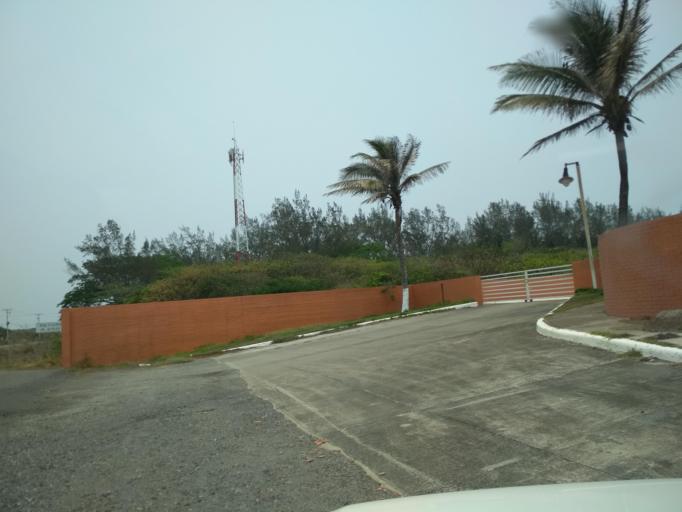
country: MX
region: Veracruz
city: Anton Lizardo
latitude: 19.0551
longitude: -96.0441
